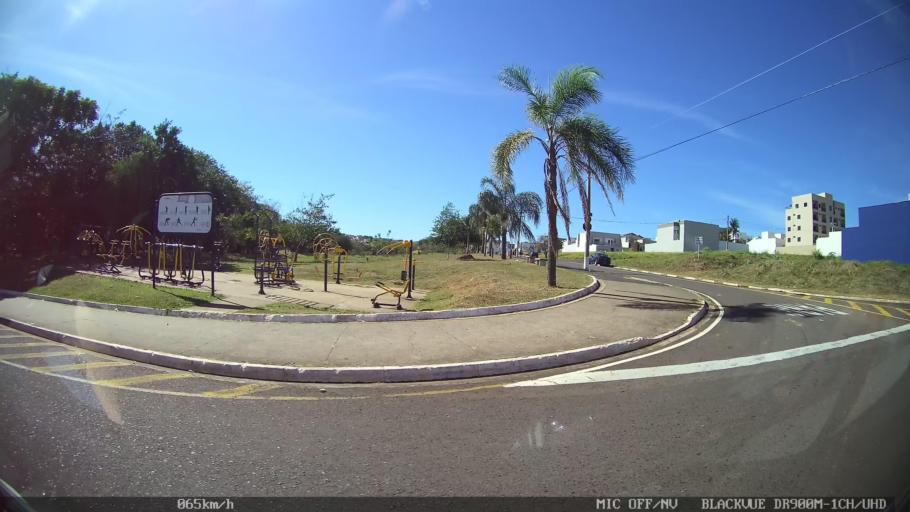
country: BR
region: Sao Paulo
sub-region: Franca
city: Franca
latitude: -20.5382
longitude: -47.3755
